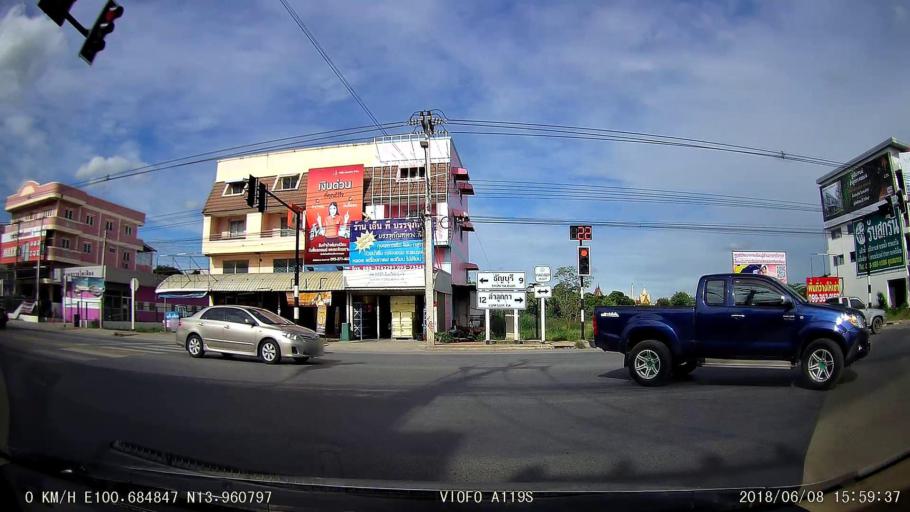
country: TH
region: Bangkok
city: Sai Mai
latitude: 13.9693
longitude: 100.6848
